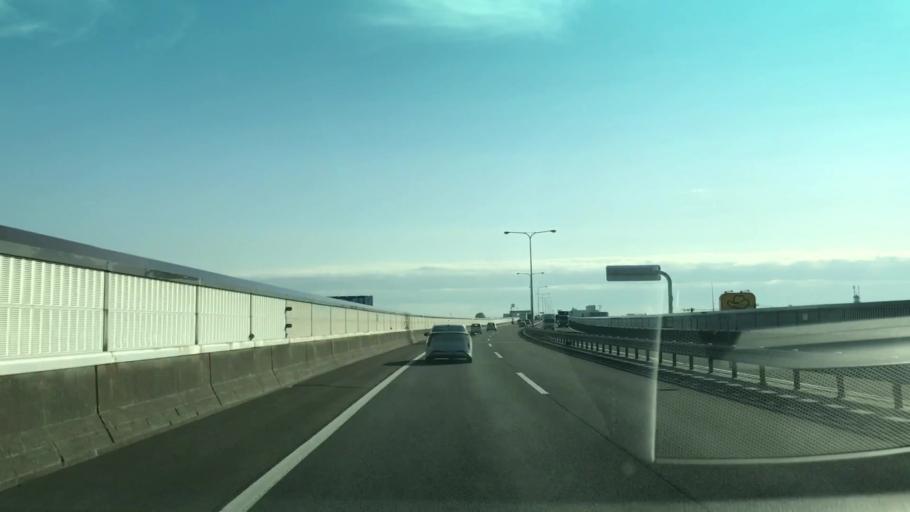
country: JP
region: Hokkaido
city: Sapporo
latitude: 43.1036
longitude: 141.3786
